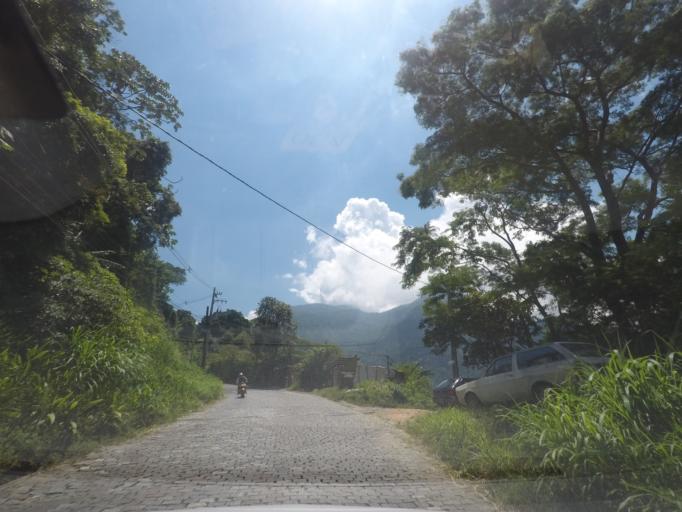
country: BR
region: Rio de Janeiro
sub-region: Petropolis
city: Petropolis
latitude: -22.5385
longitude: -43.1777
